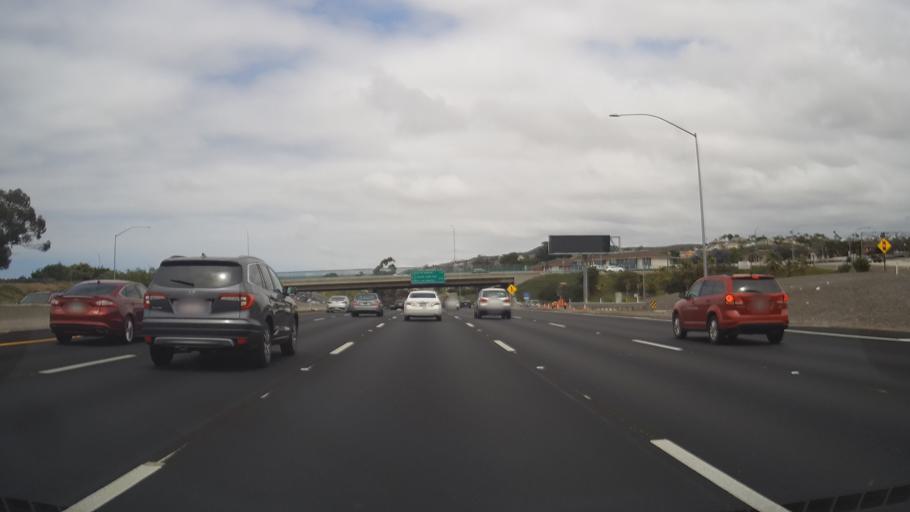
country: US
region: California
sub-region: Orange County
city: San Clemente
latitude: 33.4442
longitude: -117.6293
